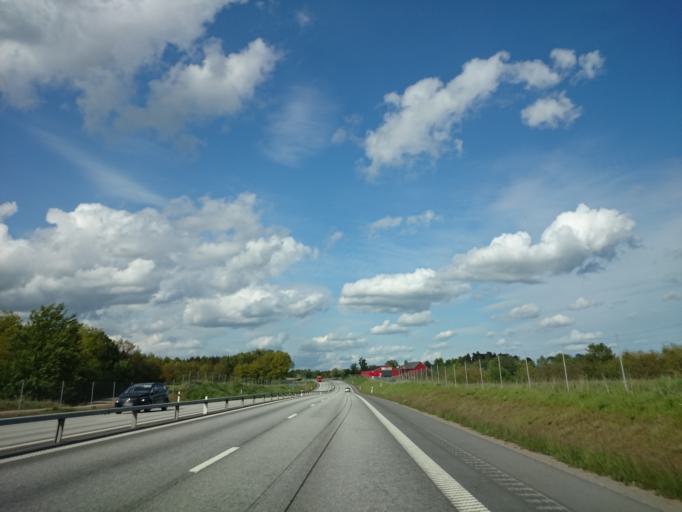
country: SE
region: Skane
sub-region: Horby Kommun
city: Hoerby
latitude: 55.8721
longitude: 13.7045
